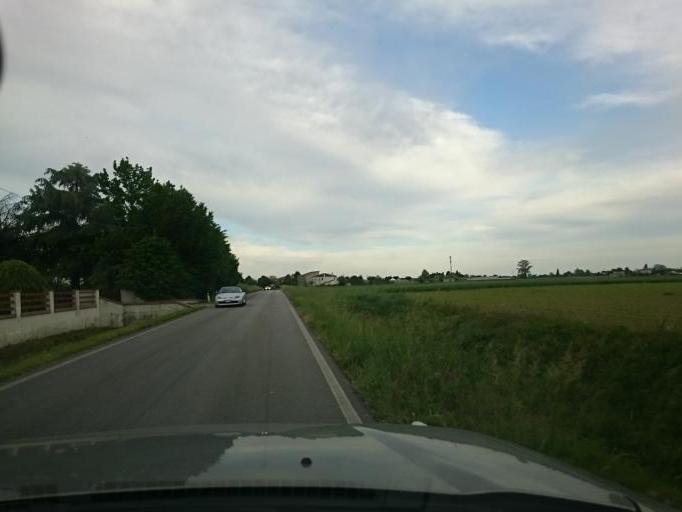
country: IT
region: Veneto
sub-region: Provincia di Padova
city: San Pietro Viminario
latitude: 45.2424
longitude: 11.8054
